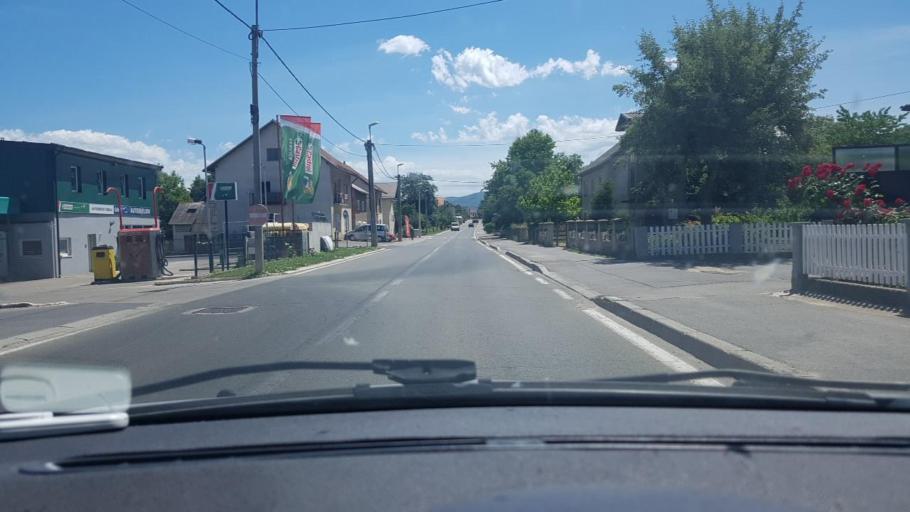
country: HR
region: Licko-Senjska
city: Otocac
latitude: 44.8673
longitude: 15.2515
